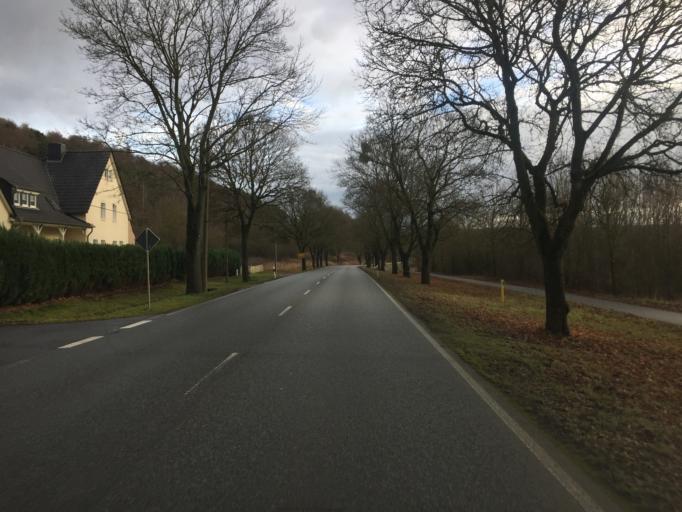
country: DE
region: Thuringia
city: Haynrode
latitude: 51.4131
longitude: 10.4624
